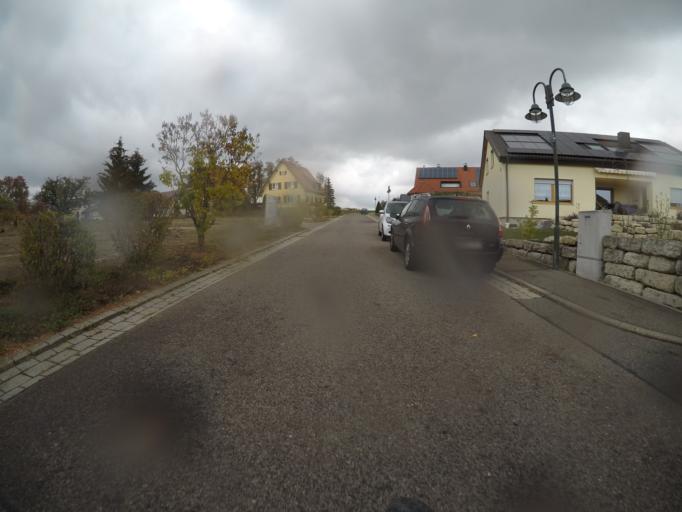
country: DE
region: Baden-Wuerttemberg
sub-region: Regierungsbezirk Stuttgart
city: Herrenberg
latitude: 48.6088
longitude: 8.8581
